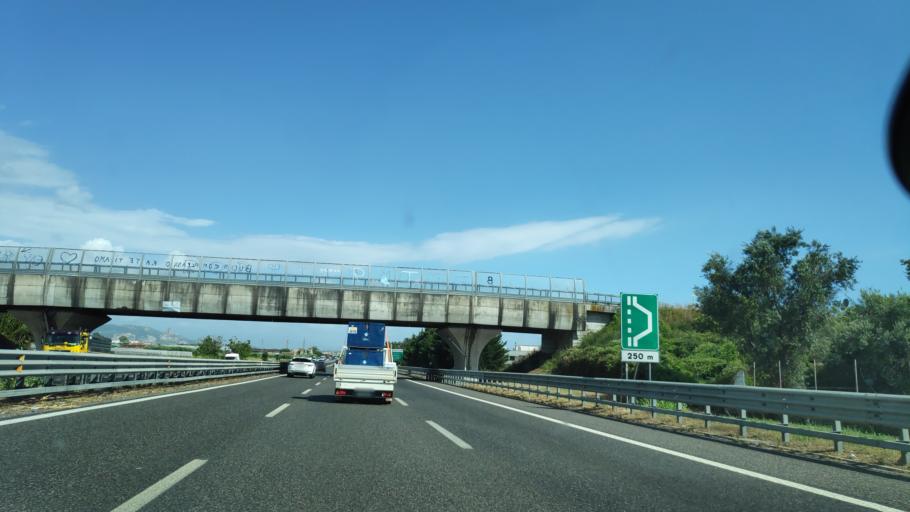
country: IT
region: Campania
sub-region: Provincia di Salerno
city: Sant'Antonio
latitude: 40.6429
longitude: 14.8949
